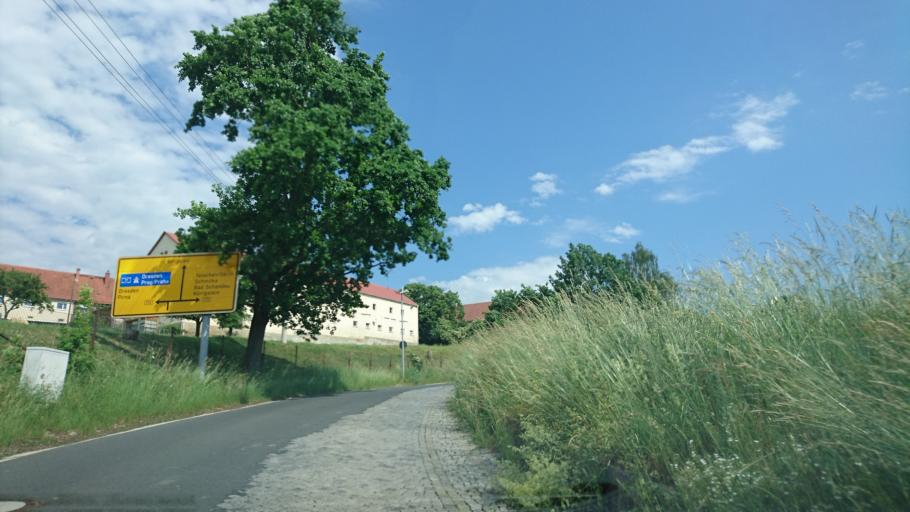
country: DE
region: Saxony
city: Struppen
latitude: 50.9269
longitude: 13.9806
